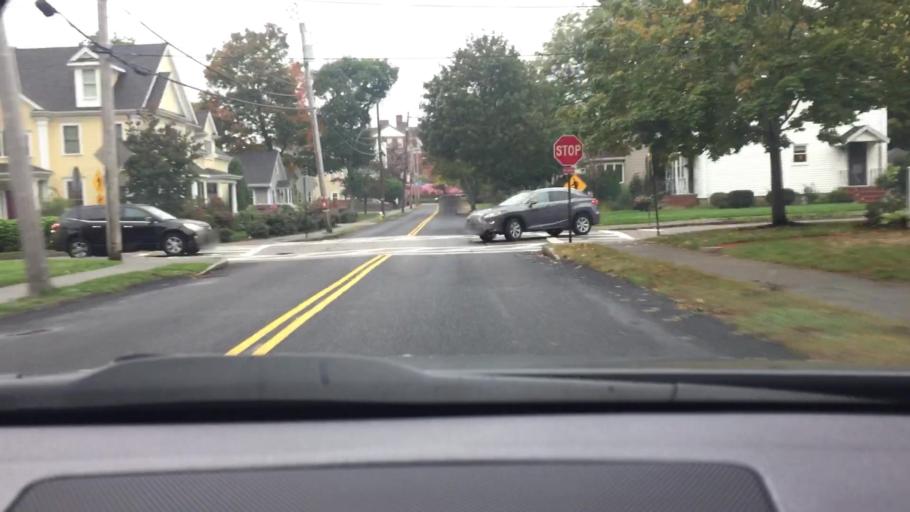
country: US
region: Massachusetts
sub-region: Norfolk County
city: Needham
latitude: 42.2867
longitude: -71.2276
